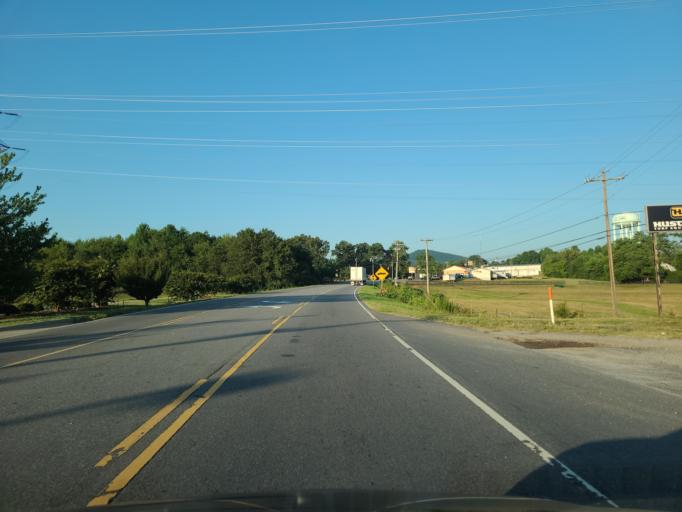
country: US
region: North Carolina
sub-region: Catawba County
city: Mountain View
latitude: 35.6824
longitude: -81.3758
